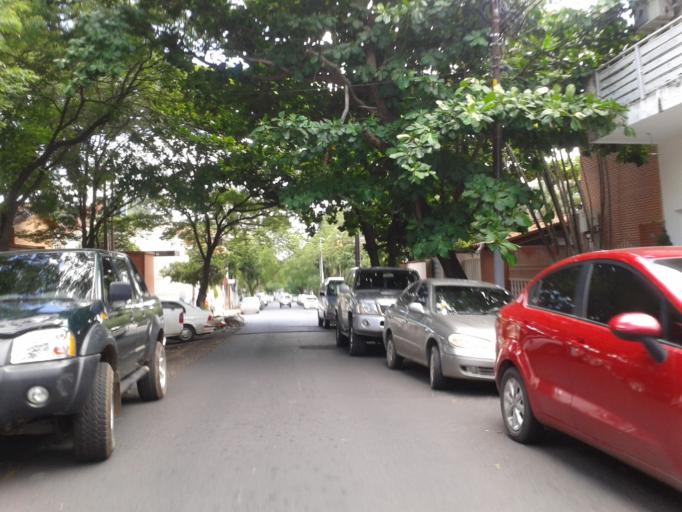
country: PY
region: Asuncion
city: Asuncion
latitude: -25.2948
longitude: -57.6168
